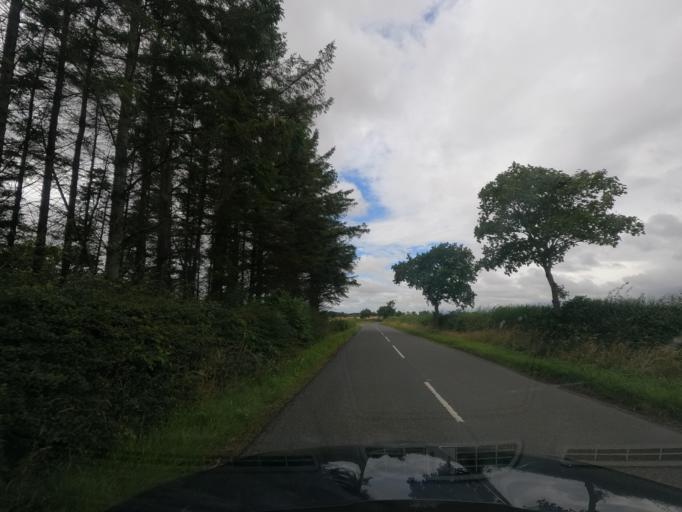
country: GB
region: Scotland
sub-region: The Scottish Borders
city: Allanton
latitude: 55.7167
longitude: -2.2020
